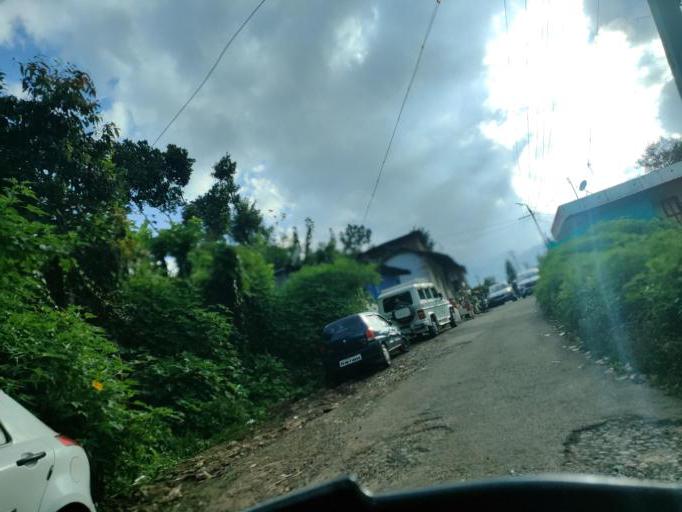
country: IN
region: Tamil Nadu
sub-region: Dindigul
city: Kodaikanal
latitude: 10.2837
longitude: 77.5311
